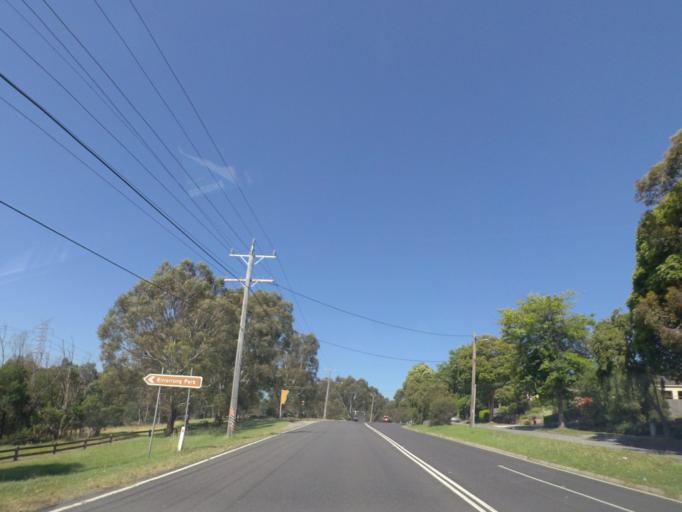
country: AU
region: Victoria
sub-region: Banyule
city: Viewbank
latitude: -37.7554
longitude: 145.0941
